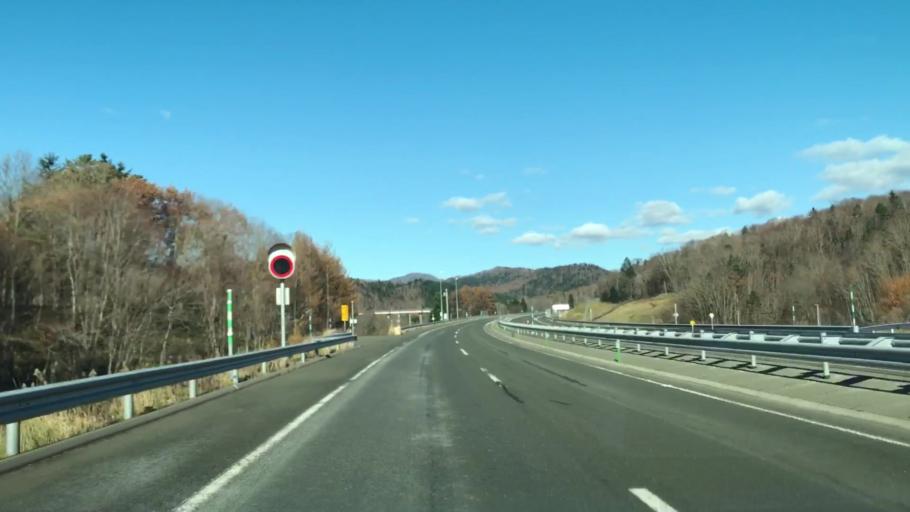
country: JP
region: Hokkaido
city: Shimo-furano
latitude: 42.9327
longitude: 142.2052
